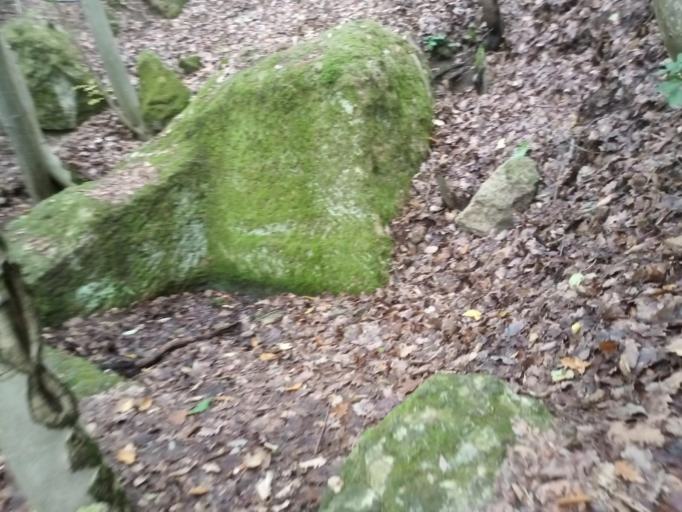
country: HU
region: Pest
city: Csobanka
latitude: 47.6748
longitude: 18.9697
